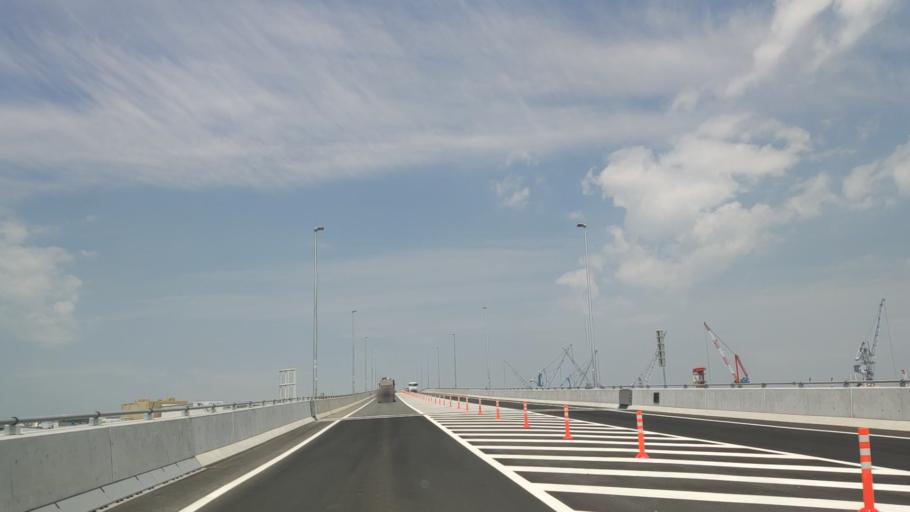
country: JP
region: Kanagawa
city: Yokohama
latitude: 35.4095
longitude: 139.6841
